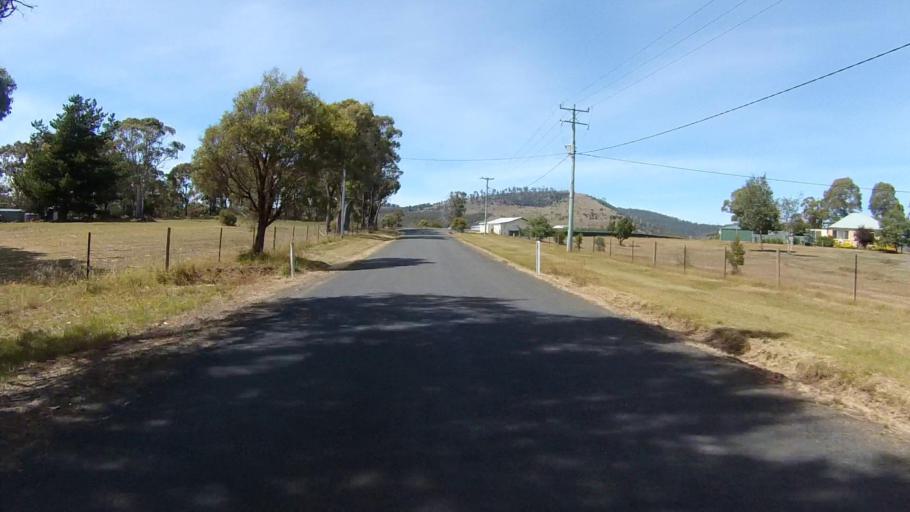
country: AU
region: Tasmania
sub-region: Sorell
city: Sorell
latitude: -42.6144
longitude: 147.7276
